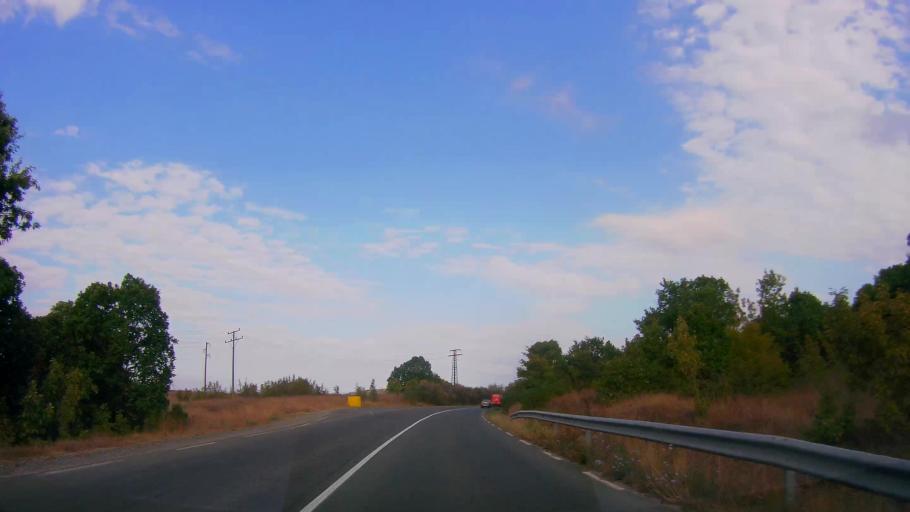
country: BG
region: Burgas
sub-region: Obshtina Sozopol
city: Sozopol
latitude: 42.3686
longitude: 27.6857
